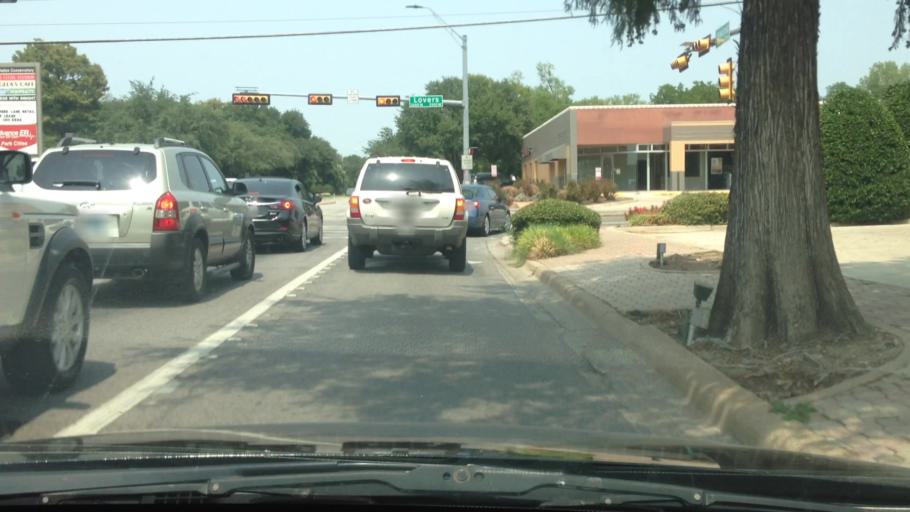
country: US
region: Texas
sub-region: Dallas County
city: University Park
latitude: 32.8508
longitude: -96.8212
